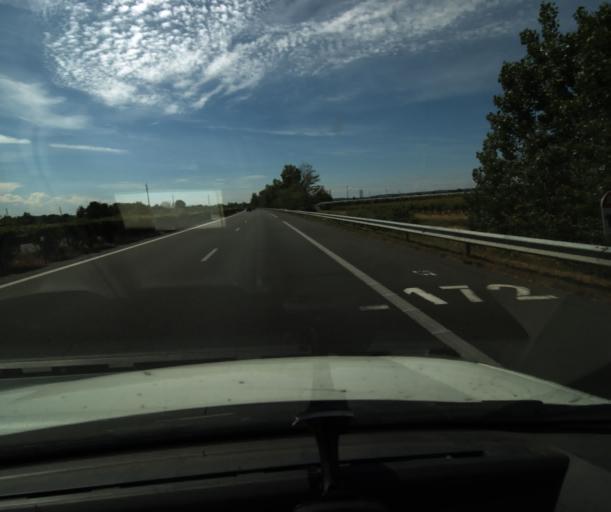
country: FR
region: Midi-Pyrenees
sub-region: Departement du Tarn-et-Garonne
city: Castelsarrasin
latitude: 44.0512
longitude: 1.1354
